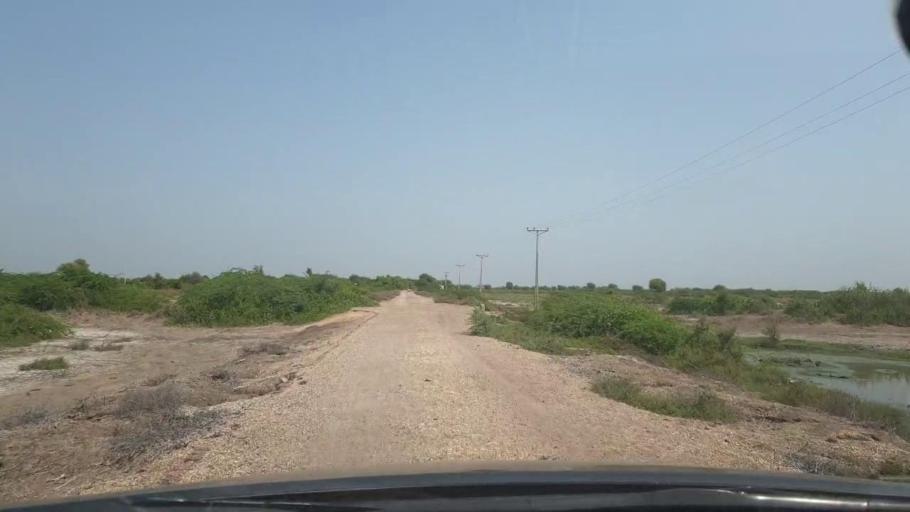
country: PK
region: Sindh
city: Naukot
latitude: 24.8032
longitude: 69.2137
